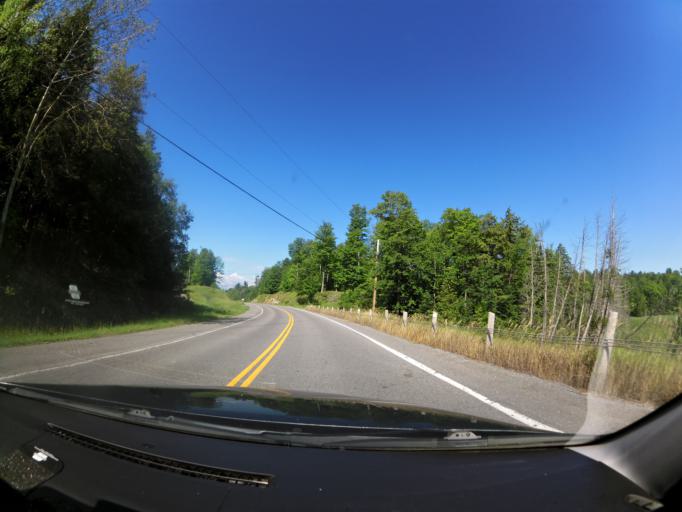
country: CA
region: Ontario
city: Carleton Place
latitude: 45.1117
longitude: -76.3673
